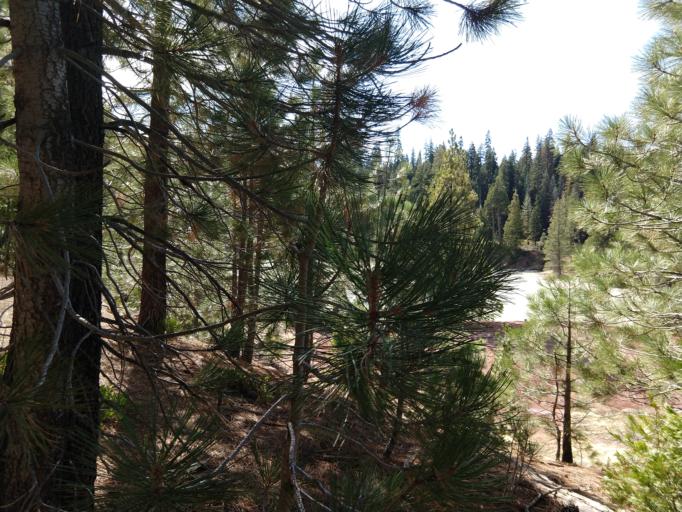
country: US
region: California
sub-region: Plumas County
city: Chester
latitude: 40.4367
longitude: -121.3975
